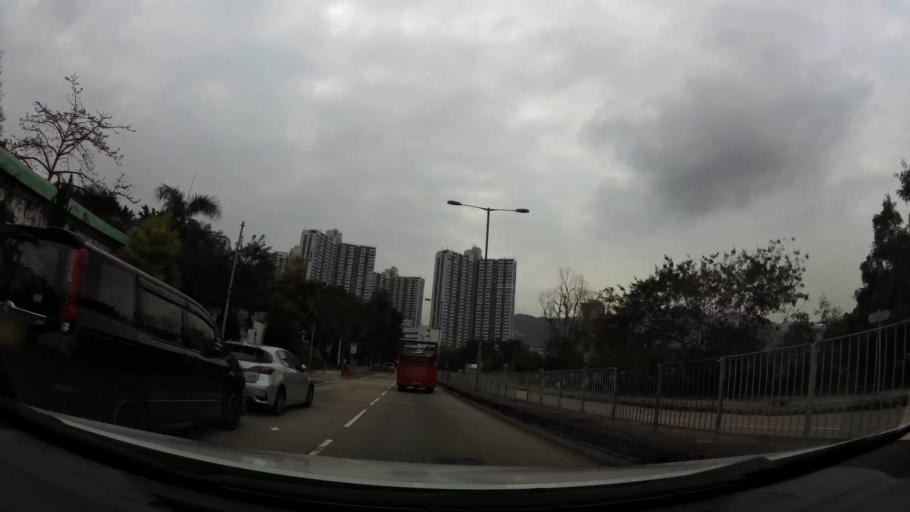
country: HK
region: Tai Po
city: Tai Po
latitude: 22.4526
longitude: 114.1795
